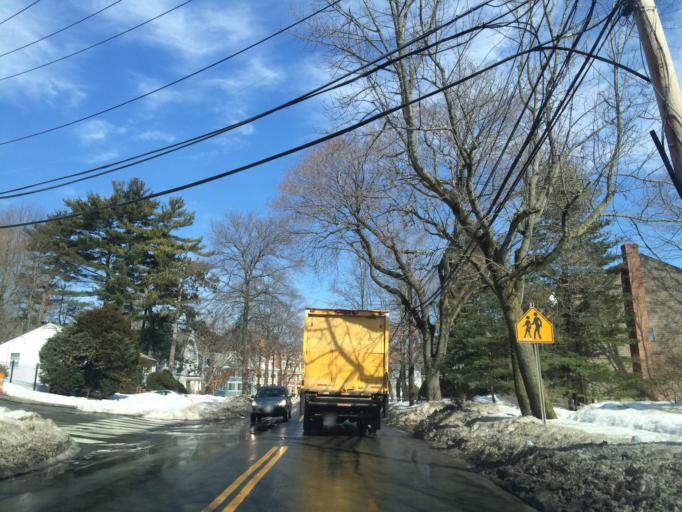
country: US
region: Massachusetts
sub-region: Middlesex County
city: Arlington
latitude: 42.4105
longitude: -71.1582
